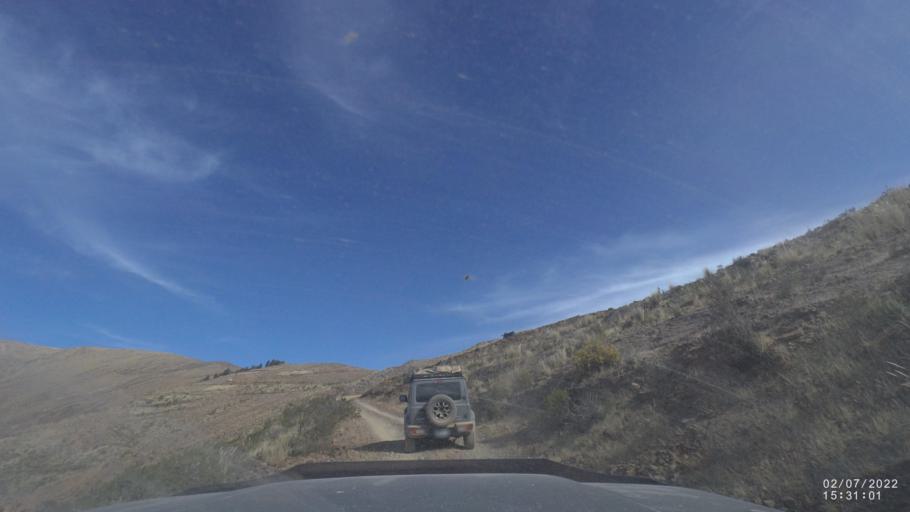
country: BO
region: Cochabamba
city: Irpa Irpa
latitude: -17.8823
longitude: -66.4139
